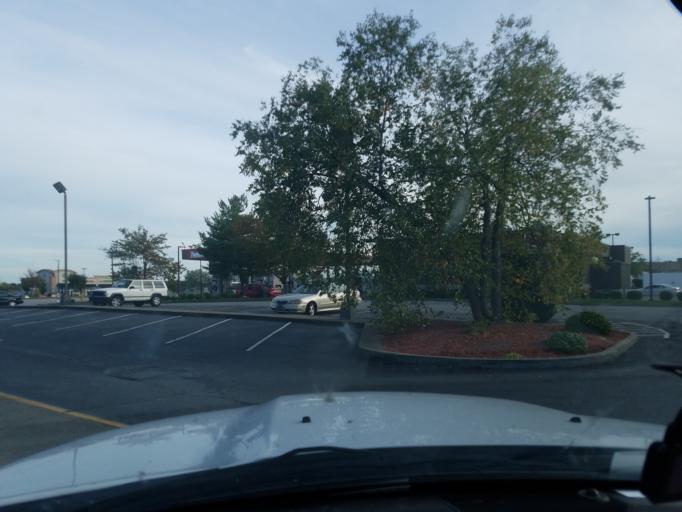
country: US
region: Kentucky
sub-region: Jefferson County
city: Douglass Hills
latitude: 38.2166
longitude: -85.5400
